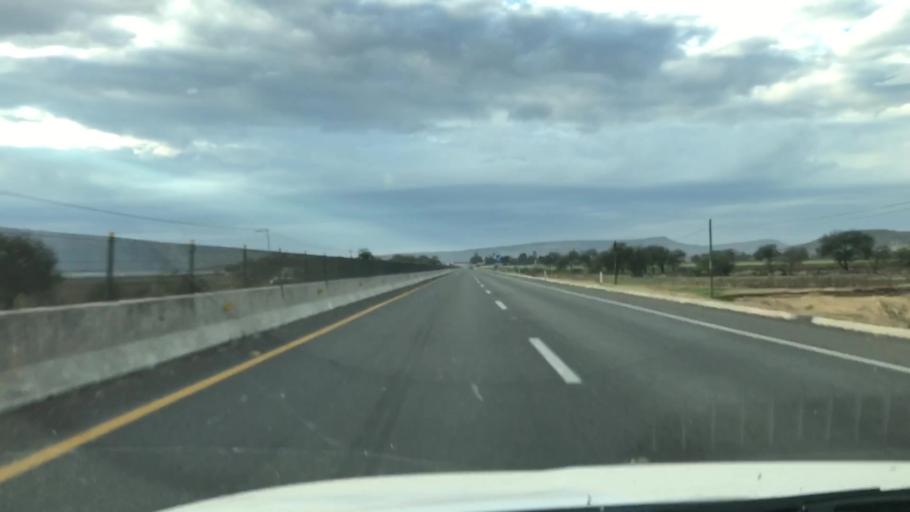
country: MX
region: Guanajuato
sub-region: Penjamo
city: Mezquite de Luna
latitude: 20.3856
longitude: -101.9098
